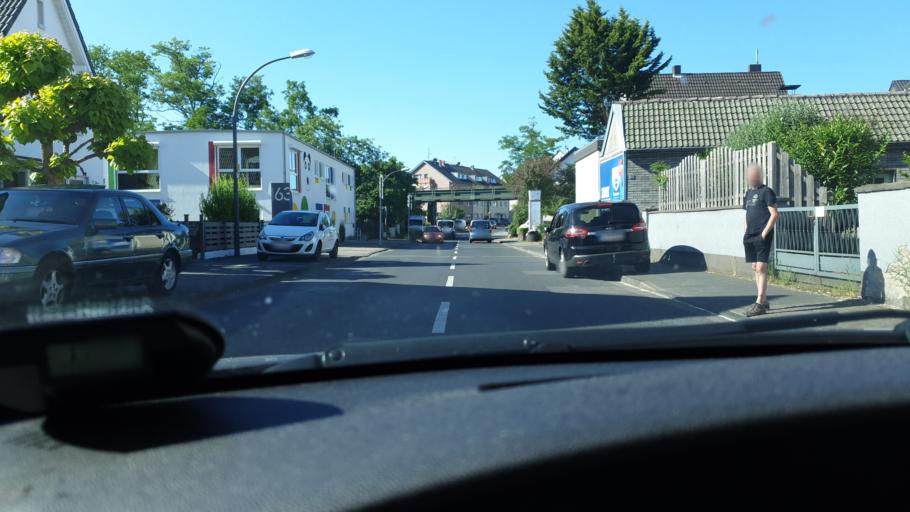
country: DE
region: North Rhine-Westphalia
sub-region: Regierungsbezirk Koln
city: Rath
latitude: 50.9153
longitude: 7.0813
